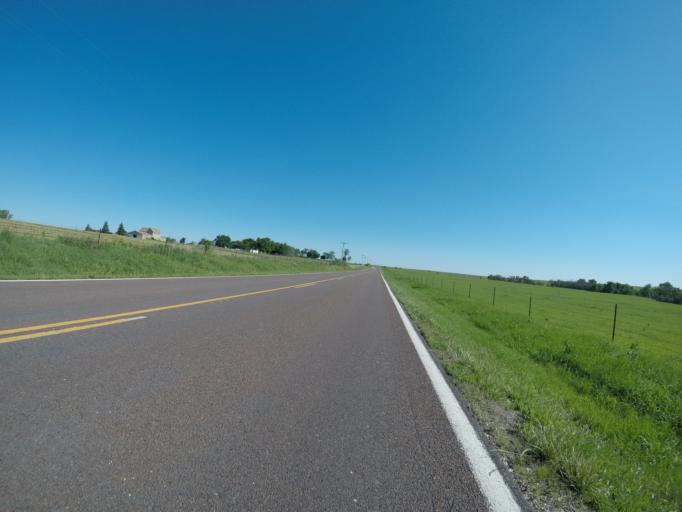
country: US
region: Kansas
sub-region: Osage County
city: Osage City
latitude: 38.6710
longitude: -96.0974
